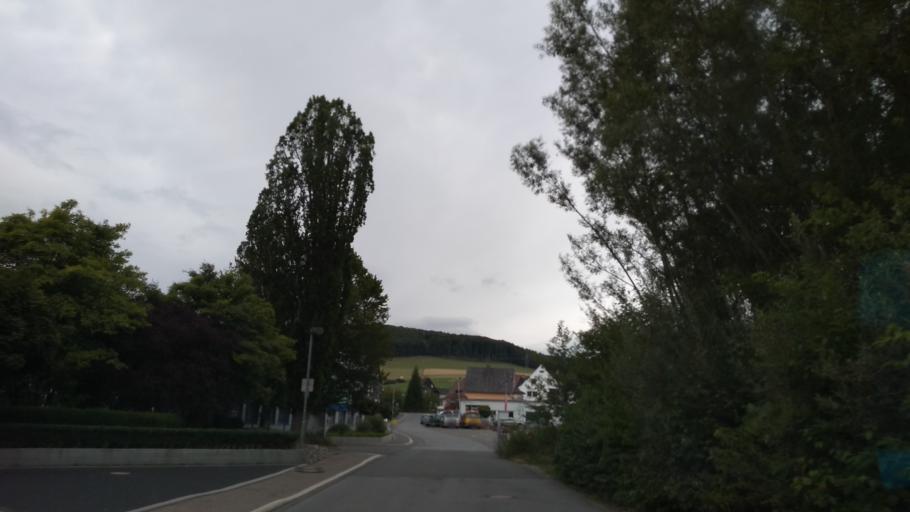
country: DE
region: North Rhine-Westphalia
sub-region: Regierungsbezirk Arnsberg
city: Herscheid
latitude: 51.1902
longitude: 7.8020
